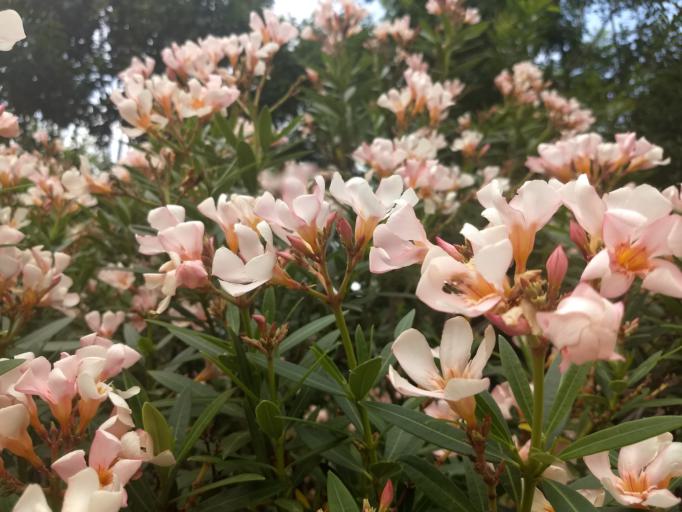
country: MX
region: Nuevo Leon
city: Santiago
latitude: 25.3664
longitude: -100.1618
